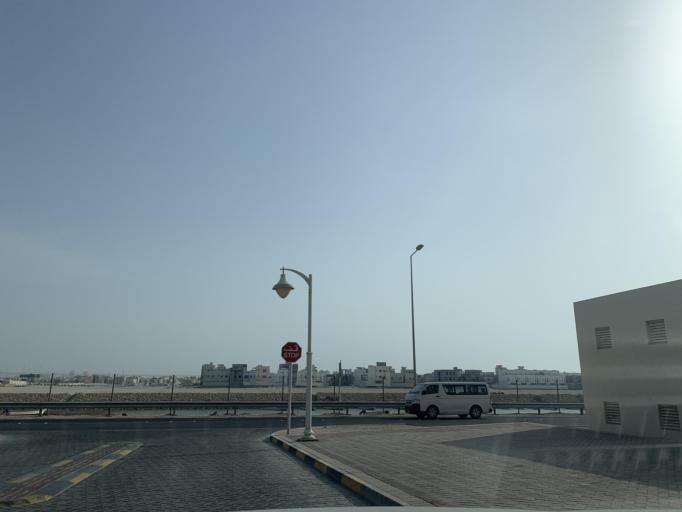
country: BH
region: Muharraq
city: Al Muharraq
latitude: 26.2956
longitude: 50.6408
